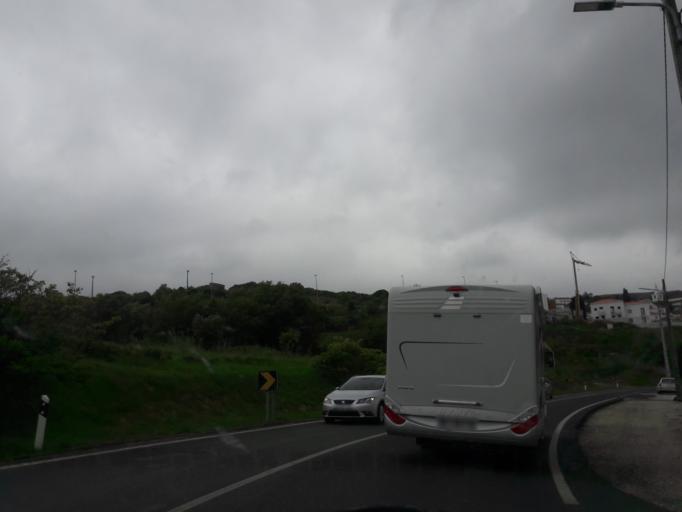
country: PT
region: Leiria
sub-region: Obidos
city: Obidos
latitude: 39.3585
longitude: -9.1532
